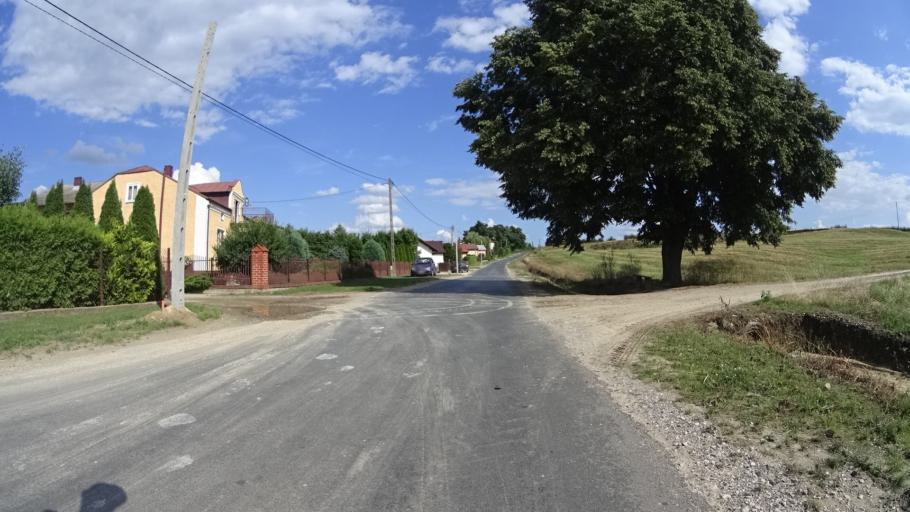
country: PL
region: Masovian Voivodeship
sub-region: Powiat grojecki
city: Mogielnica
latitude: 51.6907
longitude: 20.7439
